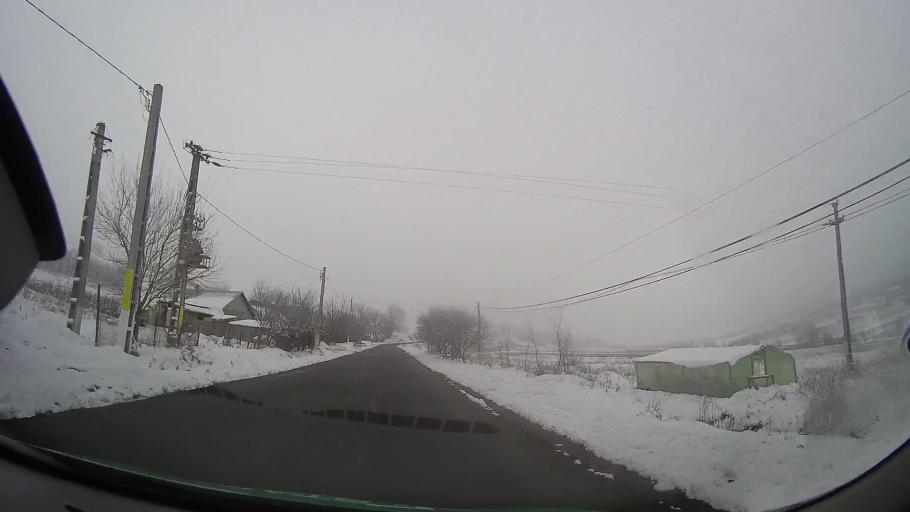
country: RO
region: Bacau
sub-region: Comuna Oncesti
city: Oncesti
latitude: 46.4844
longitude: 27.2557
